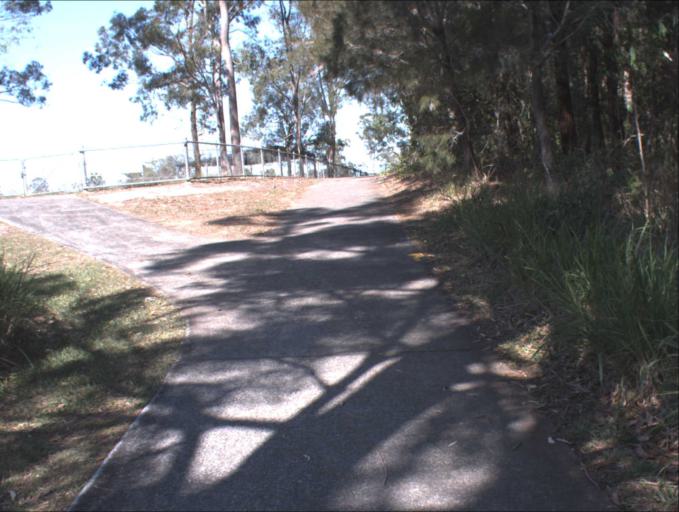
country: AU
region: Queensland
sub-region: Logan
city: Slacks Creek
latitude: -27.6385
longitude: 153.1321
